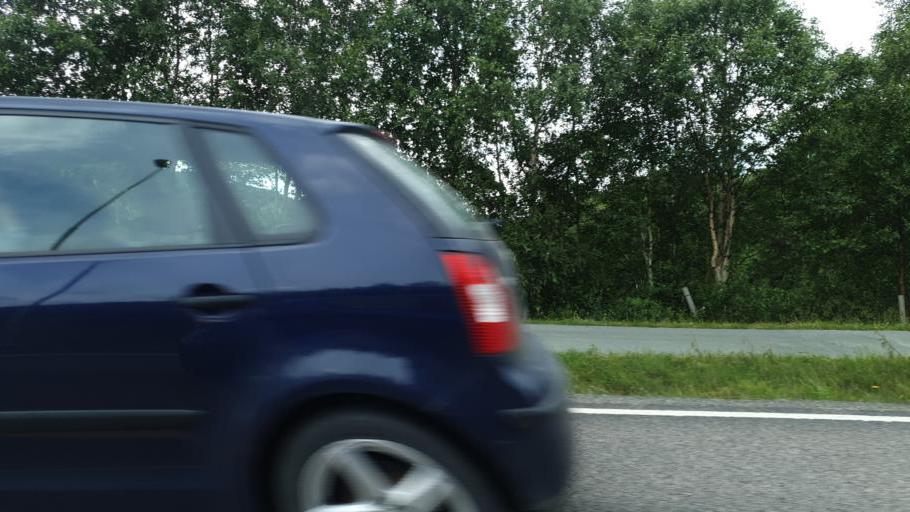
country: NO
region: Sor-Trondelag
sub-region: Oppdal
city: Oppdal
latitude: 62.5772
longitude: 9.6551
